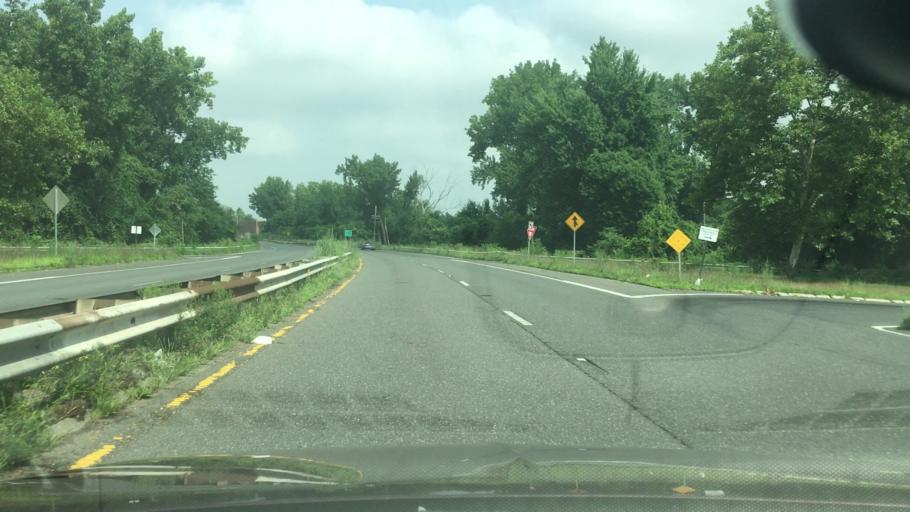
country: US
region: Massachusetts
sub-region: Hampden County
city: Springfield
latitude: 42.0927
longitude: -72.5926
